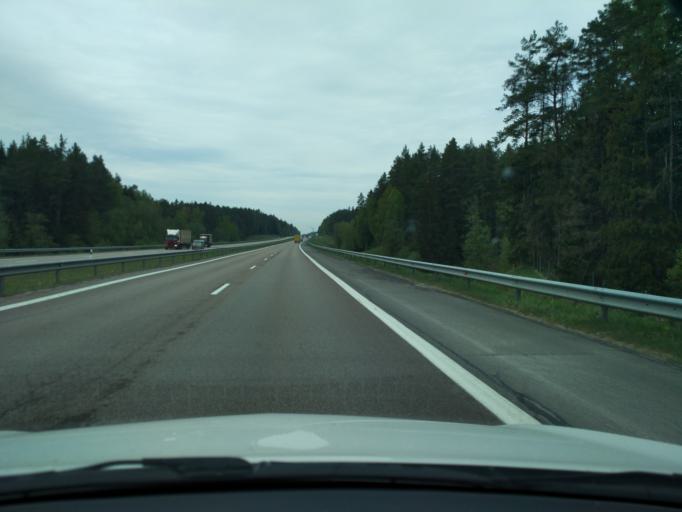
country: LT
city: Sirvintos
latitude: 54.9558
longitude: 24.9593
